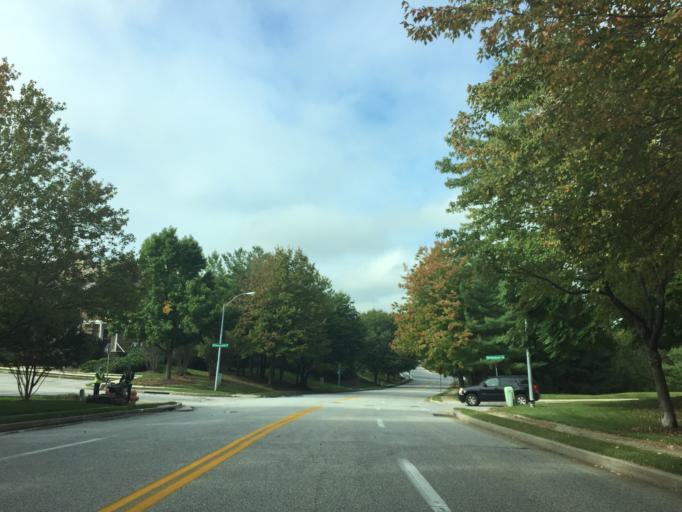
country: US
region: Maryland
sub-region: Baltimore County
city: Pikesville
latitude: 39.3814
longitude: -76.6830
